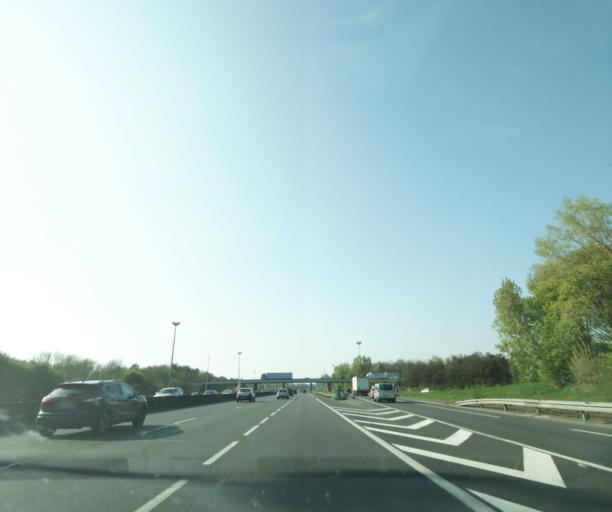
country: FR
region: Ile-de-France
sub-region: Departement de l'Essonne
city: Ris-Orangis
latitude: 48.6342
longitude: 2.4034
